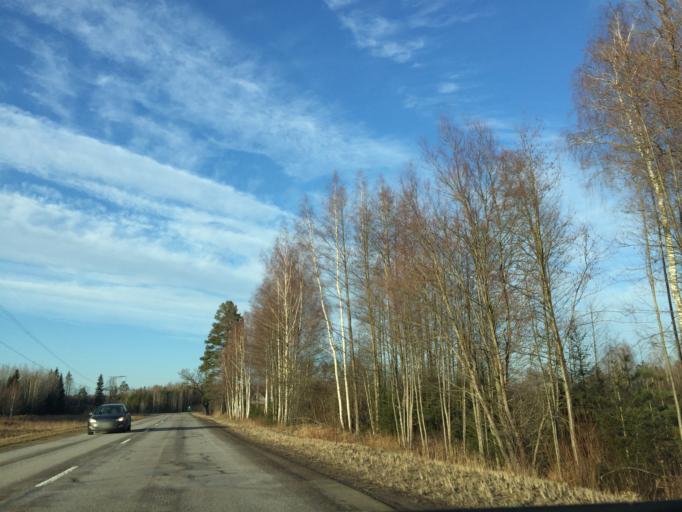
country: LV
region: Kekava
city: Balozi
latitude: 56.7975
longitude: 24.0752
